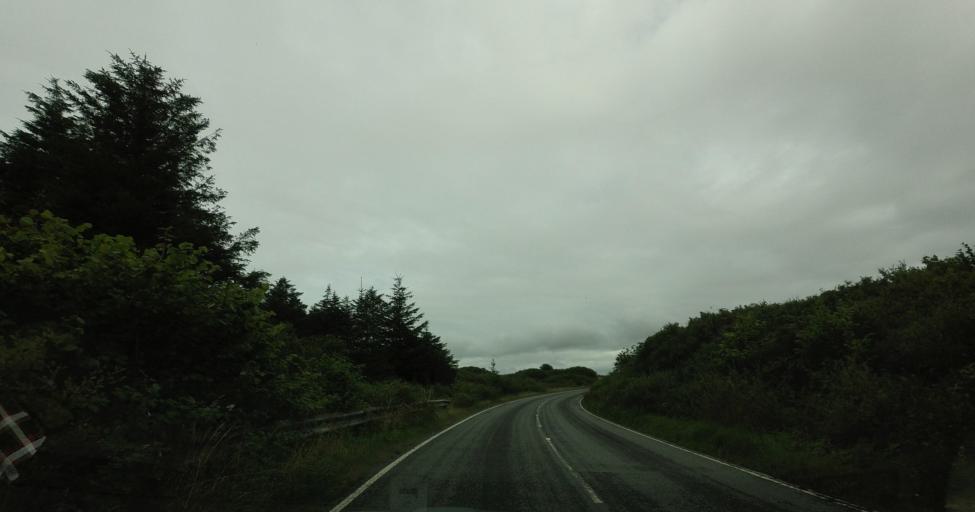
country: GB
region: Scotland
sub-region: Highland
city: Isle of Skye
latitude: 57.4144
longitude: -6.5279
